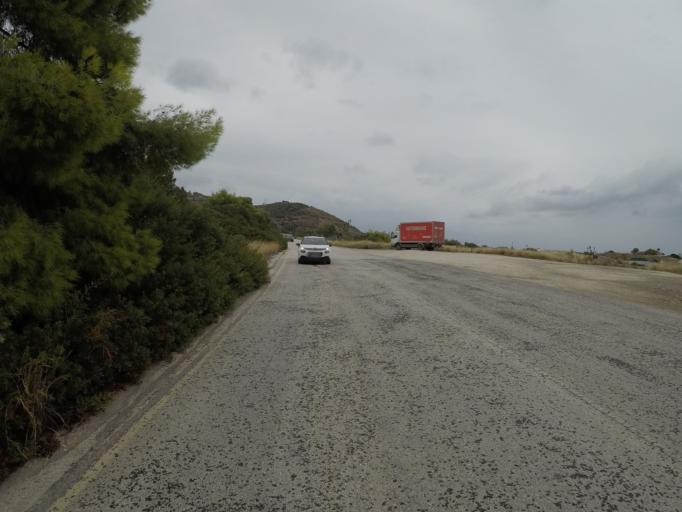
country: GR
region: Peloponnese
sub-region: Nomos Korinthias
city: Agioi Theodoroi
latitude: 37.9193
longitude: 23.0910
